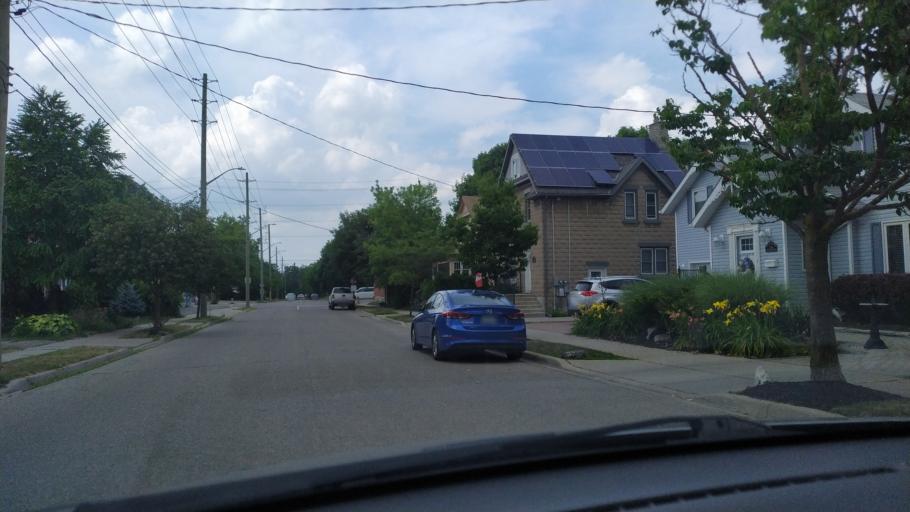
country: CA
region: Ontario
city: Waterloo
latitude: 43.4608
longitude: -80.5314
